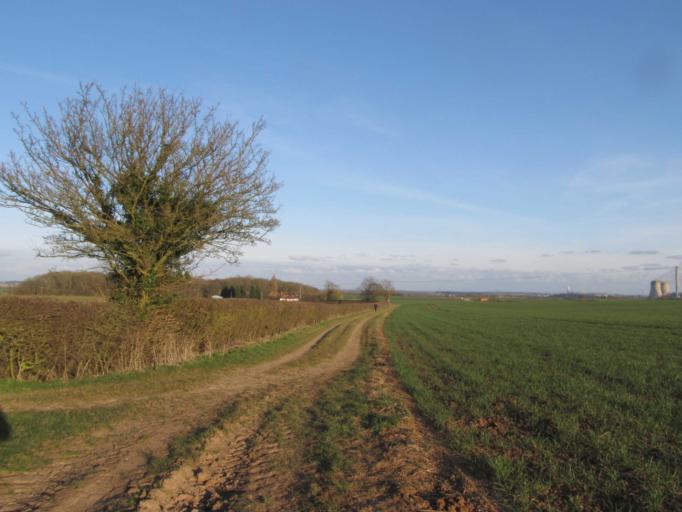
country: GB
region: England
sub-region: Nottinghamshire
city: Misterton
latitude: 53.3870
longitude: -0.8524
